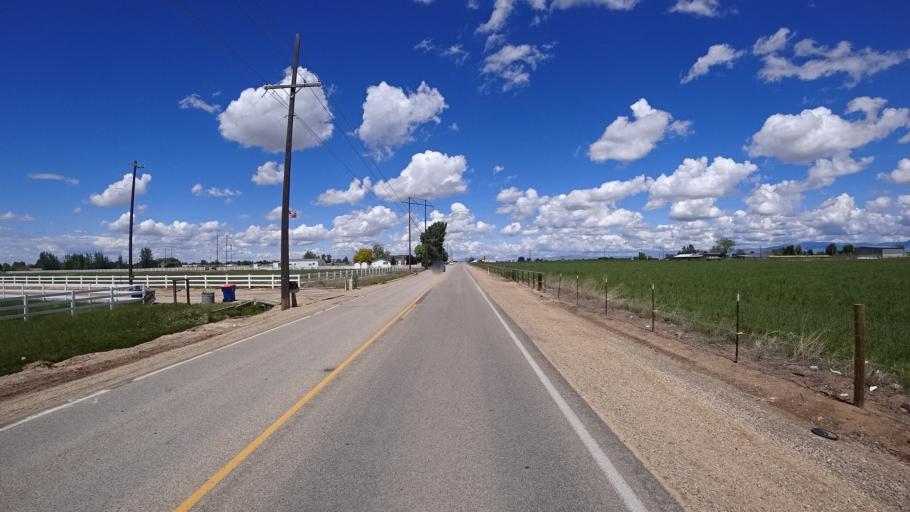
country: US
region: Idaho
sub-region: Ada County
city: Kuna
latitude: 43.5583
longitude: -116.4338
